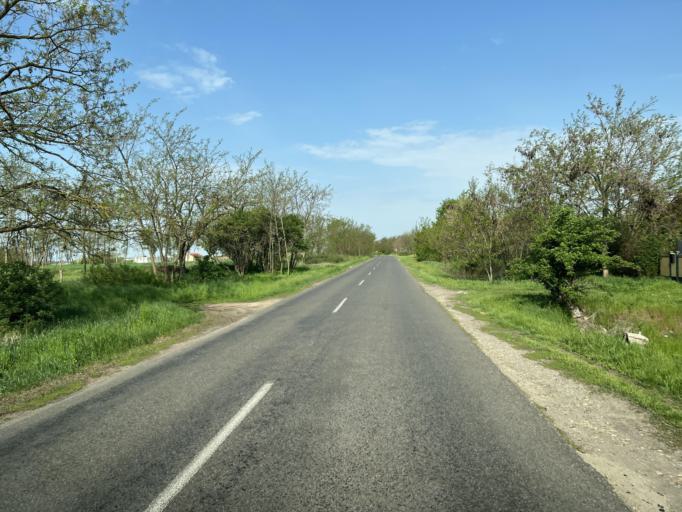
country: HU
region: Pest
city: Jaszkarajeno
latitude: 47.0415
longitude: 20.1026
